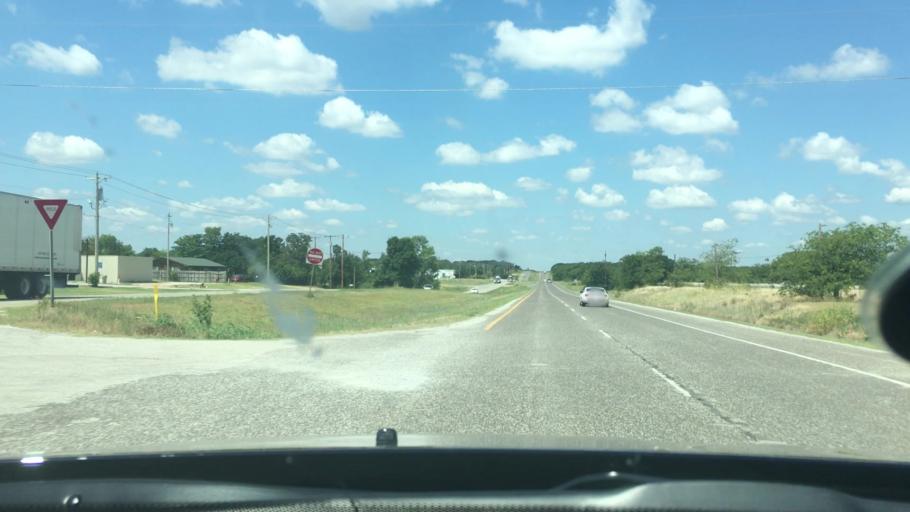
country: US
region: Oklahoma
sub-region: Carter County
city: Lone Grove
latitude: 34.1731
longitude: -97.2782
